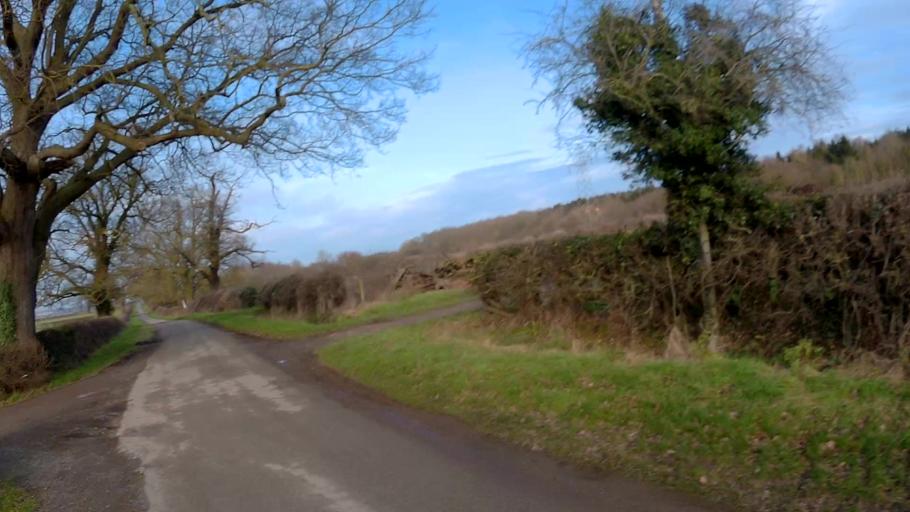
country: GB
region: England
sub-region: Lincolnshire
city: Bourne
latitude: 52.7626
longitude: -0.4195
